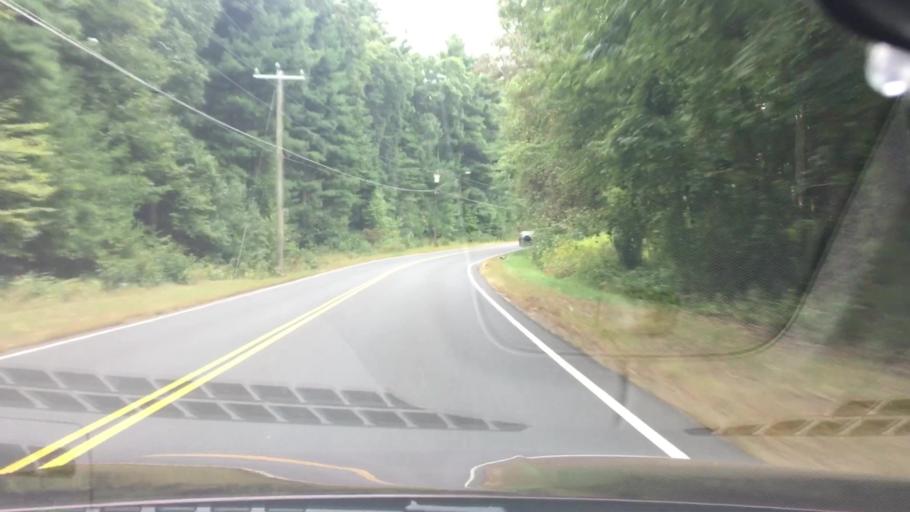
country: US
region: Connecticut
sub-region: Hartford County
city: Sherwood Manor
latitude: 42.0173
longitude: -72.5597
